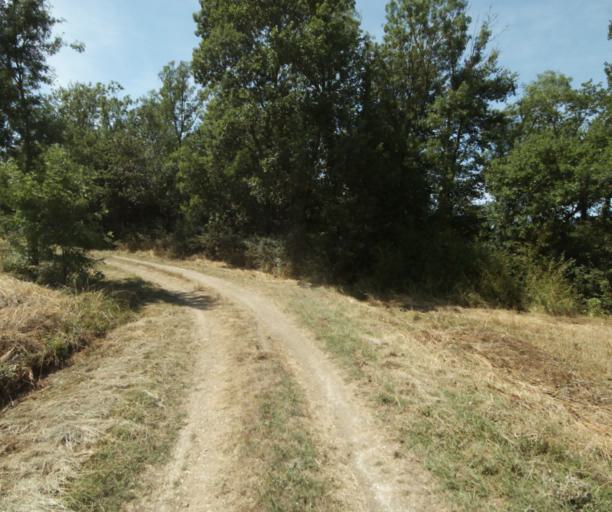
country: FR
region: Midi-Pyrenees
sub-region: Departement de la Haute-Garonne
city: Revel
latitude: 43.5134
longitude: 2.0140
